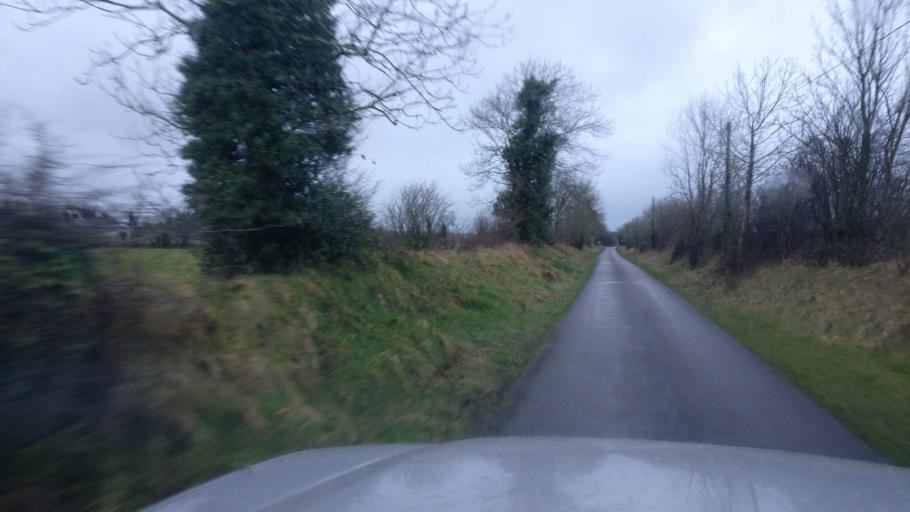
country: IE
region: Connaught
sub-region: County Galway
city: Ballinasloe
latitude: 53.2761
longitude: -8.3367
